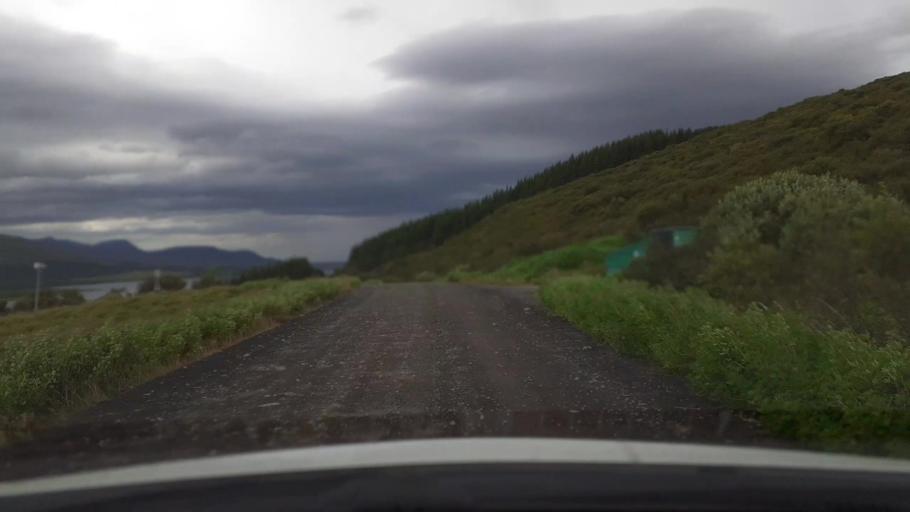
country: IS
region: Capital Region
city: Mosfellsbaer
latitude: 64.5273
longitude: -21.4926
